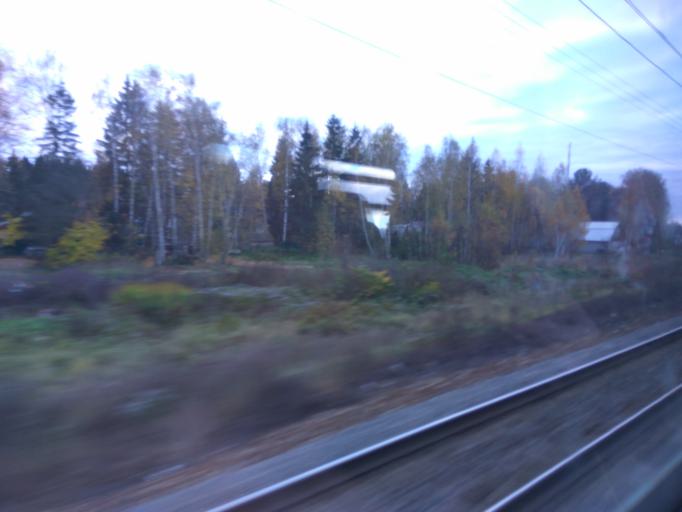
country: RU
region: Moskovskaya
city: Aprelevka
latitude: 55.5424
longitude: 37.0414
